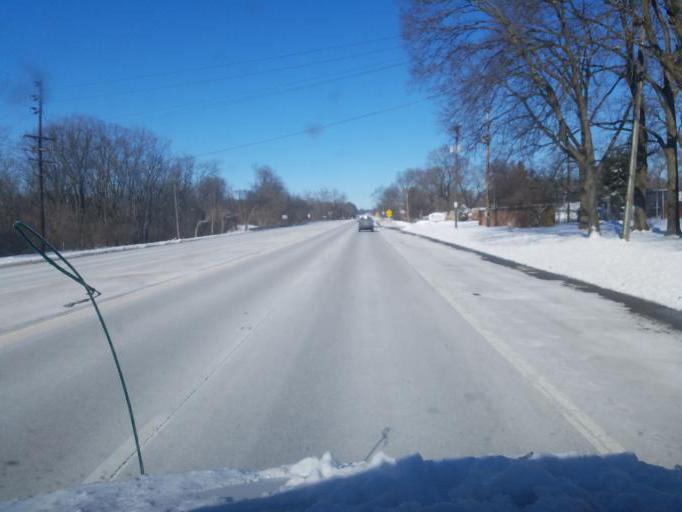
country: US
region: Ohio
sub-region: Delaware County
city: Delaware
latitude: 40.2526
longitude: -83.0605
